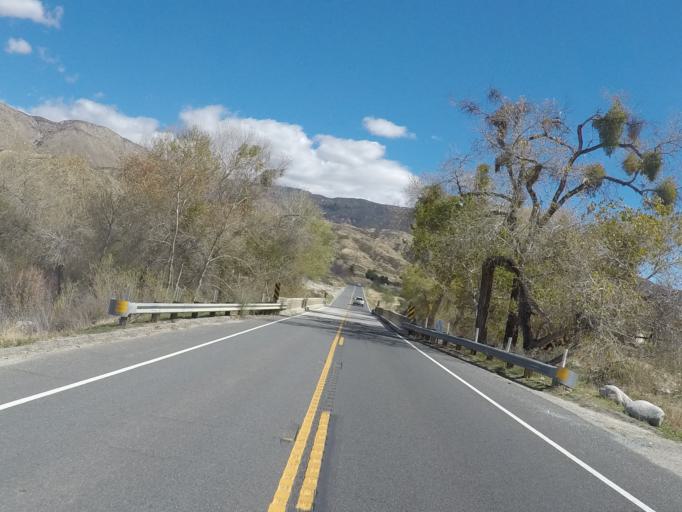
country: US
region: California
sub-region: Riverside County
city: Valle Vista
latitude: 33.7368
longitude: -116.8271
